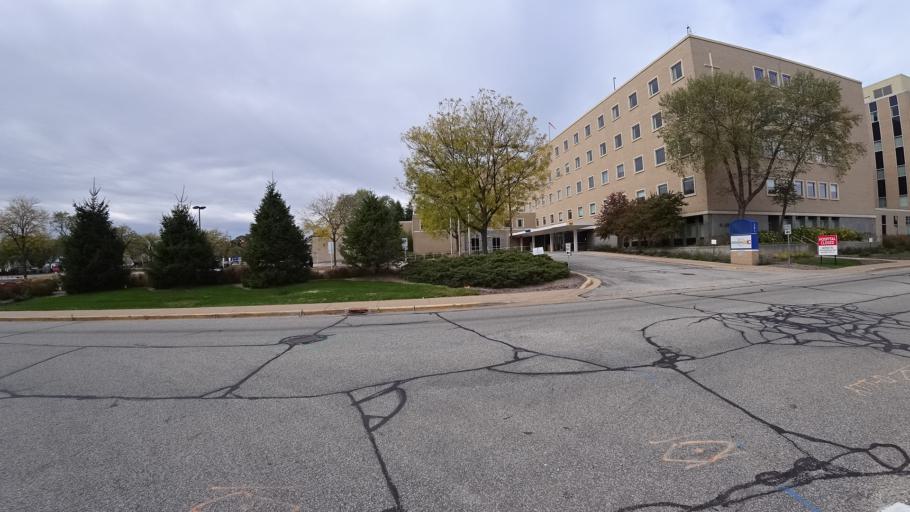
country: US
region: Indiana
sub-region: LaPorte County
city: Michigan City
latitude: 41.7063
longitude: -86.8997
